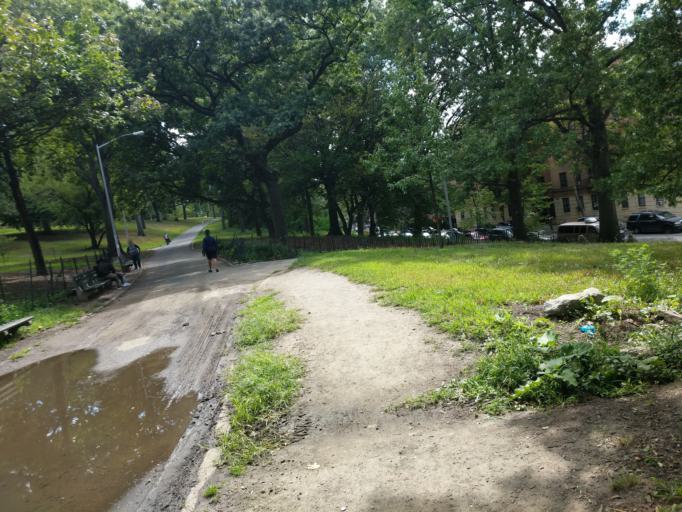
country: US
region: New York
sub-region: New York County
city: Inwood
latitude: 40.8402
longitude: -73.9087
